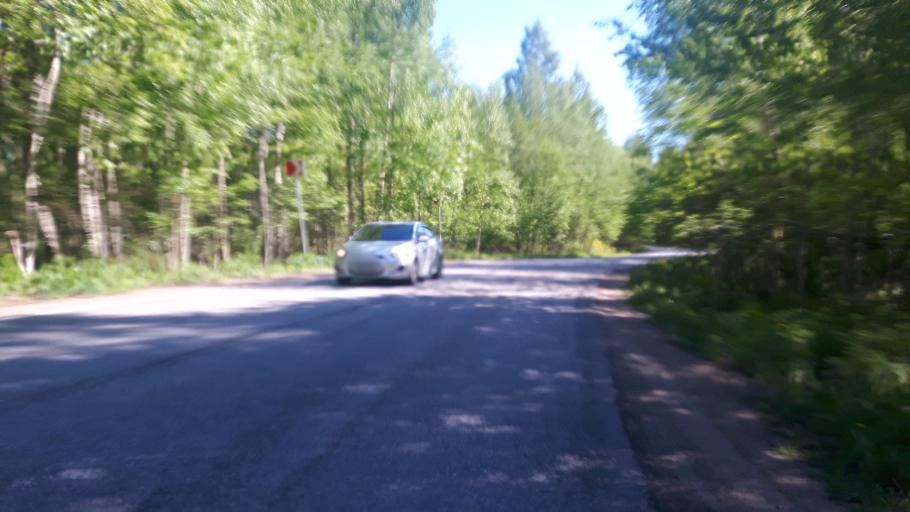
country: RU
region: Leningrad
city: Glebychevo
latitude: 60.2861
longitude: 28.8773
